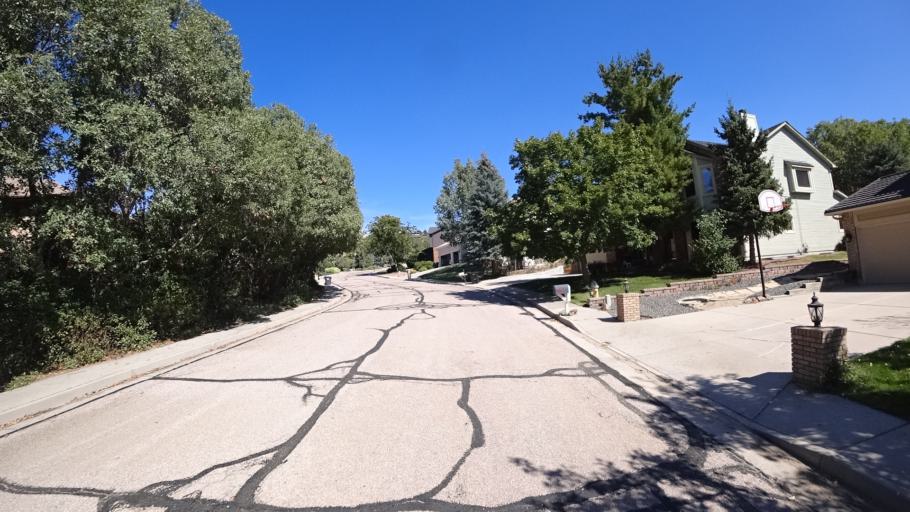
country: US
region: Colorado
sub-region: El Paso County
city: Cimarron Hills
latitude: 38.9134
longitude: -104.7529
